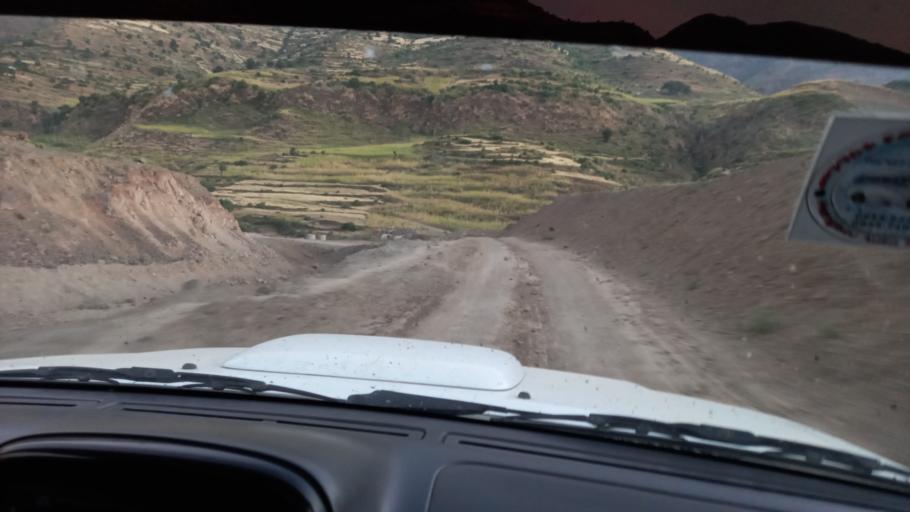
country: ET
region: Amhara
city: Debark'
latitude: 13.0313
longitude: 38.0540
